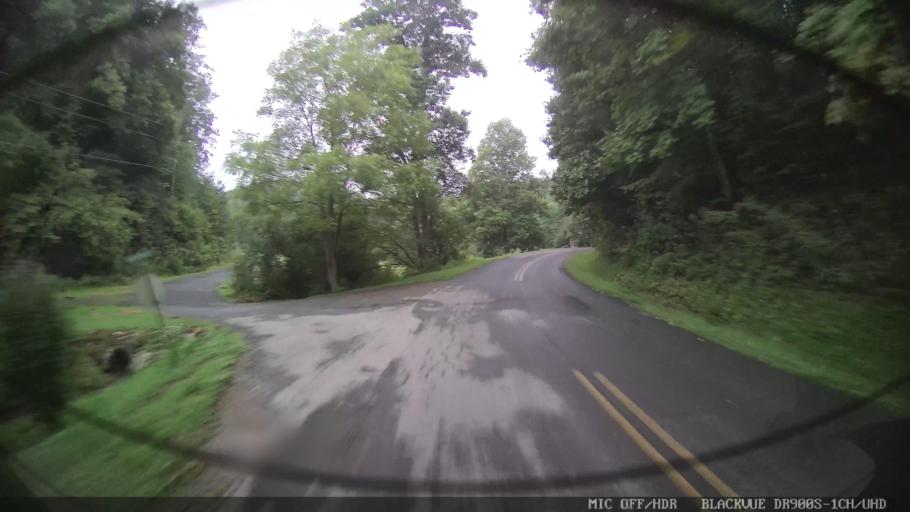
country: US
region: Georgia
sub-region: Gilmer County
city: Ellijay
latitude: 34.7867
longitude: -84.5533
